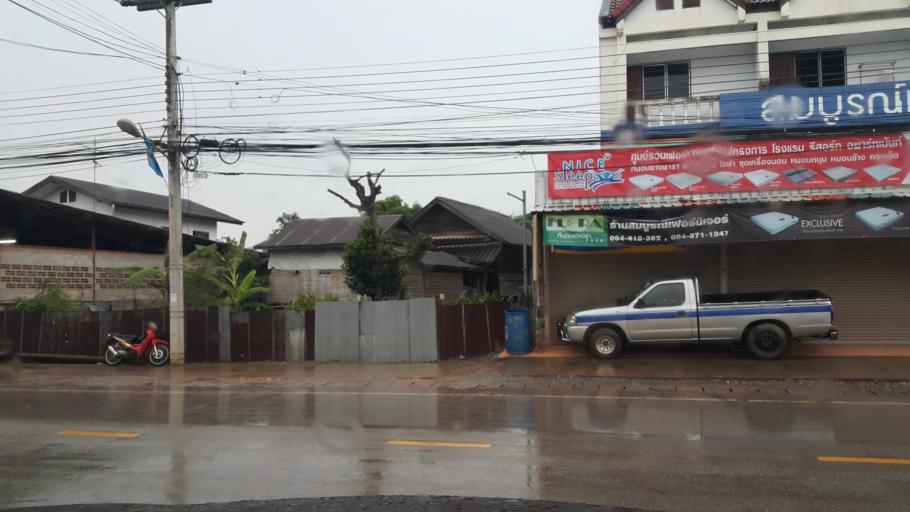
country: TH
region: Phayao
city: Chiang Kham
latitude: 19.5184
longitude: 100.3006
